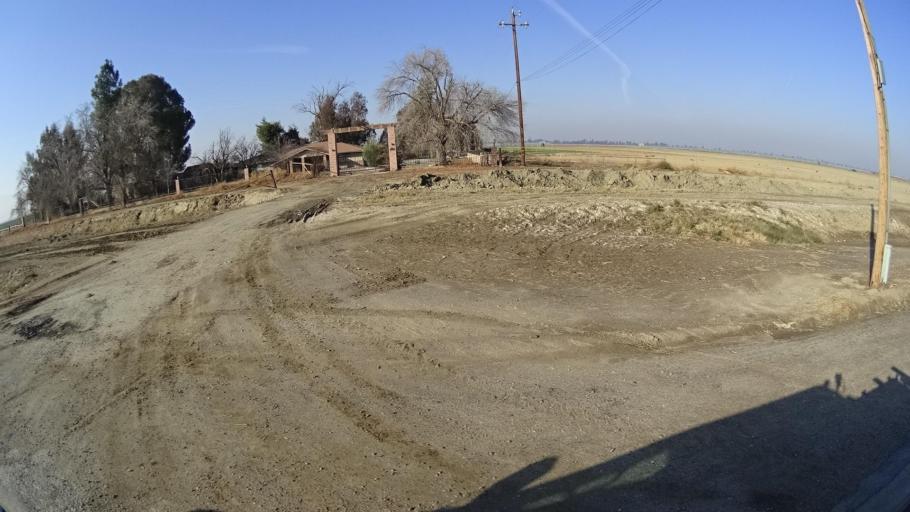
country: US
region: California
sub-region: Kern County
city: Weedpatch
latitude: 35.1868
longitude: -118.9676
